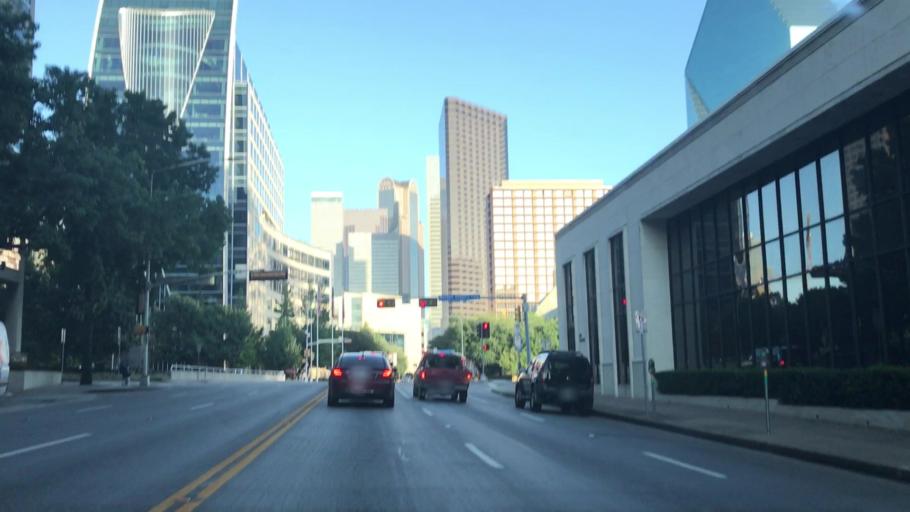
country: US
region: Texas
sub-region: Dallas County
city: Dallas
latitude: 32.7886
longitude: -96.8042
